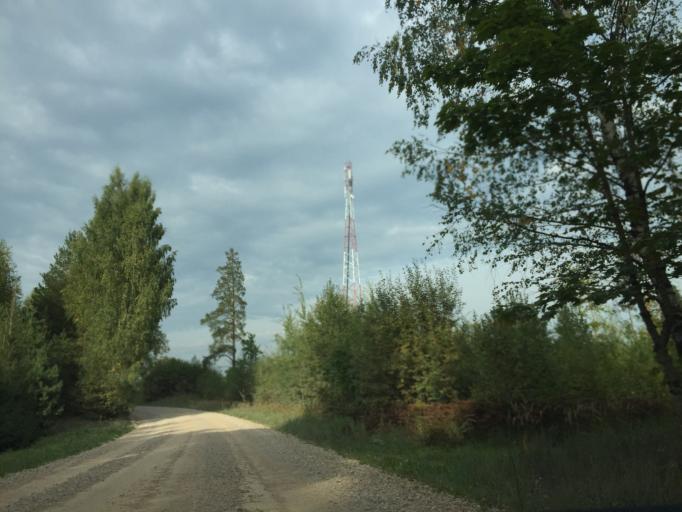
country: LV
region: Ikskile
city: Ikskile
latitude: 56.8098
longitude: 24.4465
